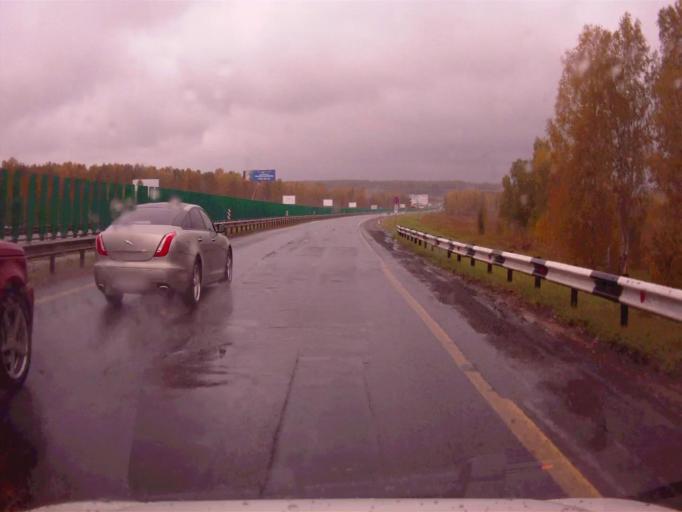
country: RU
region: Chelyabinsk
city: Dolgoderevenskoye
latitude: 55.3404
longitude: 61.3064
